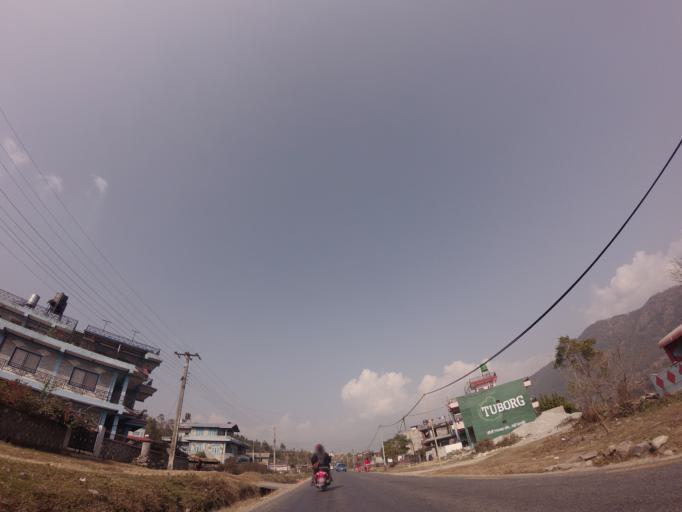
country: NP
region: Western Region
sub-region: Gandaki Zone
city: Pokhara
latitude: 28.2639
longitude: 83.9565
